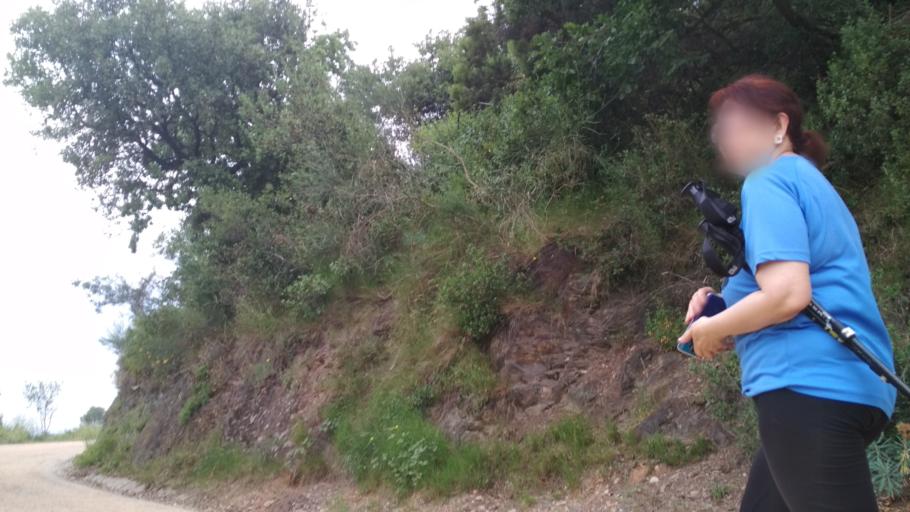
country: ES
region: Catalonia
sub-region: Provincia de Barcelona
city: Nou Barris
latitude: 41.4511
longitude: 2.1631
